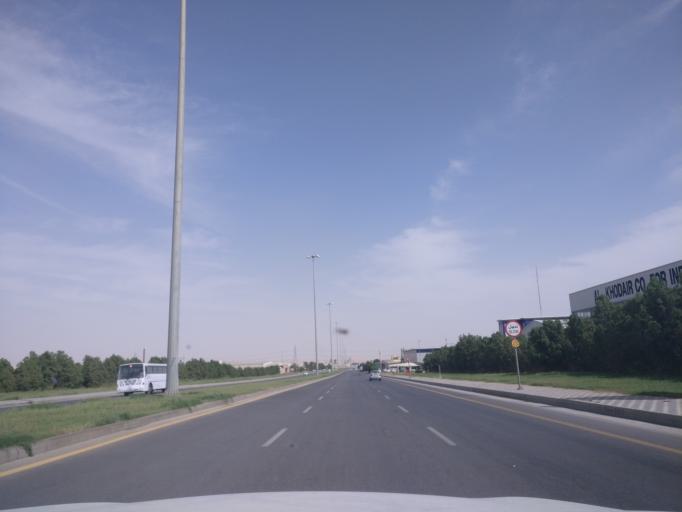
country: SA
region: Ar Riyad
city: Riyadh
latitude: 24.5301
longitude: 46.9104
